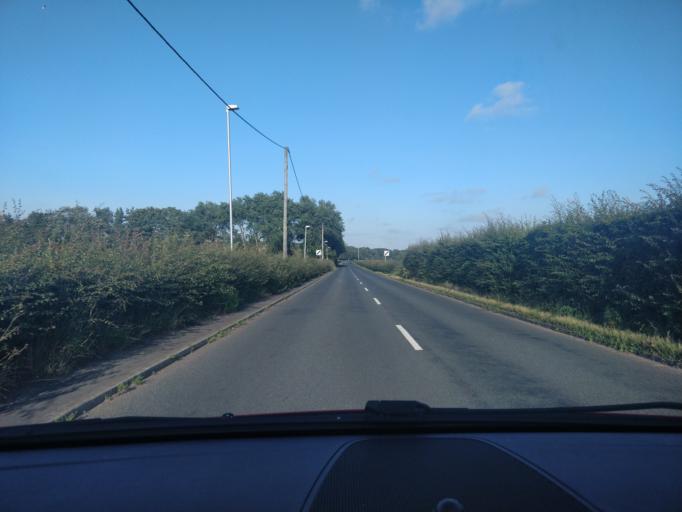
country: GB
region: England
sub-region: Lancashire
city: Tarleton
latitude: 53.6403
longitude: -2.8429
